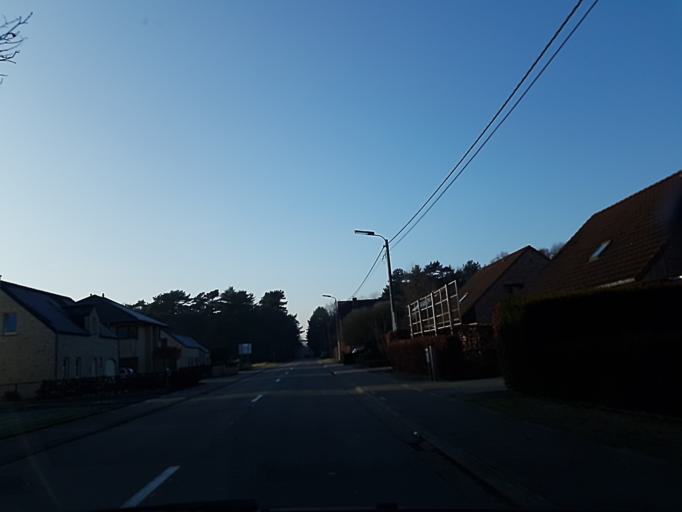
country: BE
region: Flanders
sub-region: Provincie Vlaams-Brabant
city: Tremelo
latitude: 51.0150
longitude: 4.7240
